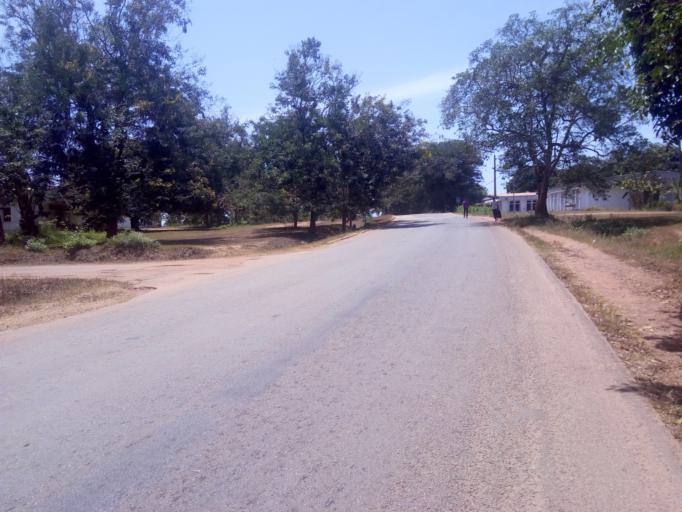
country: GH
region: Central
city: Cape Coast
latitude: 5.1284
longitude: -1.2916
